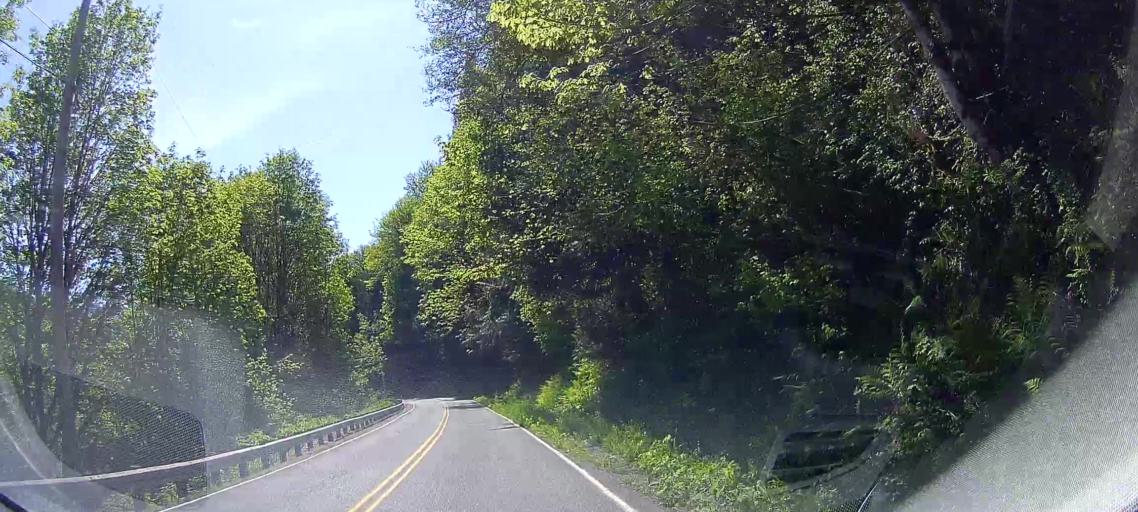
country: US
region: Washington
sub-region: Snohomish County
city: Darrington
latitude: 48.4771
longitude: -121.6472
